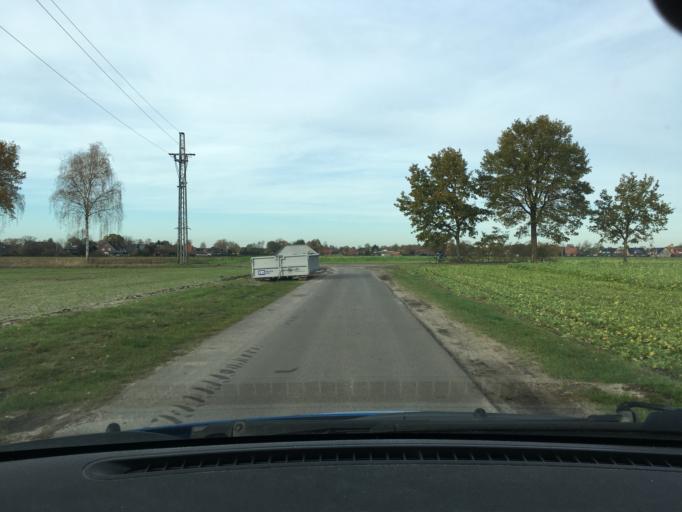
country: DE
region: Lower Saxony
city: Wittorf
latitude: 53.3237
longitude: 10.3702
